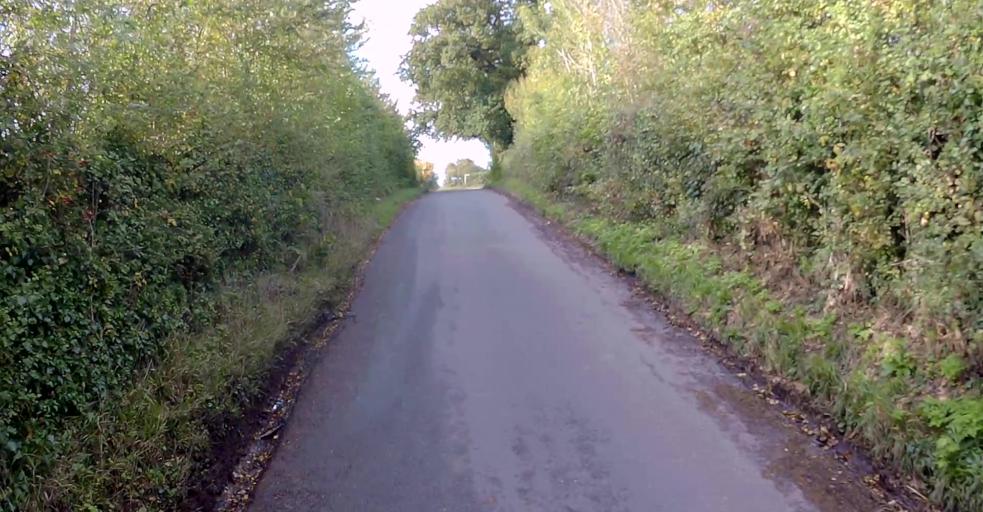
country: GB
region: England
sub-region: Surrey
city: Farnham
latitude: 51.2077
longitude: -0.8281
